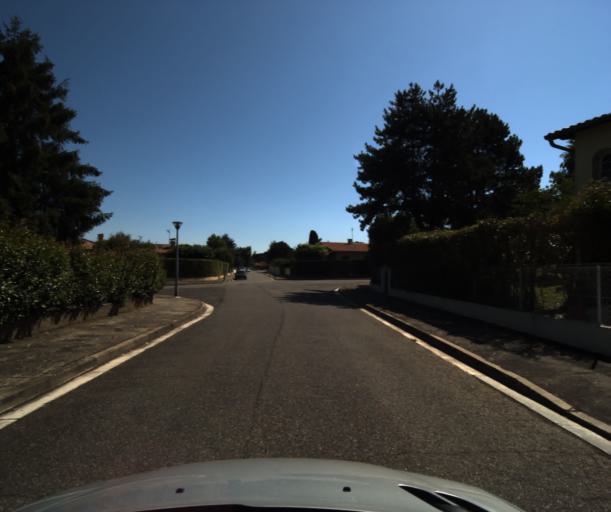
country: FR
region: Midi-Pyrenees
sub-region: Departement de la Haute-Garonne
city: Roquettes
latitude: 43.5007
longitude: 1.3670
